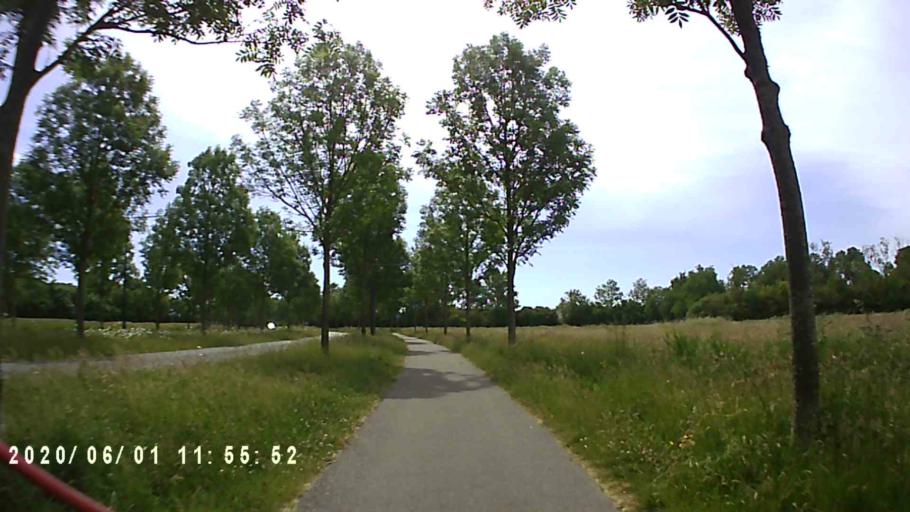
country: NL
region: Friesland
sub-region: Gemeente Harlingen
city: Harlingen
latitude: 53.1620
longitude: 5.4333
